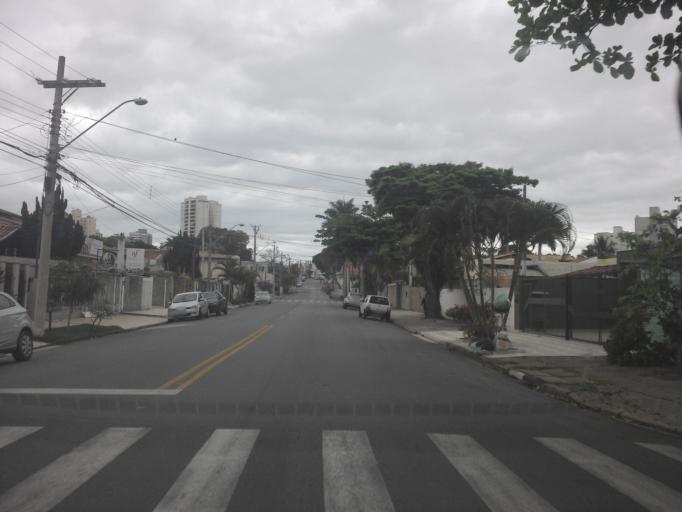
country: BR
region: Sao Paulo
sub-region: Taubate
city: Taubate
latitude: -23.0345
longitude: -45.5765
